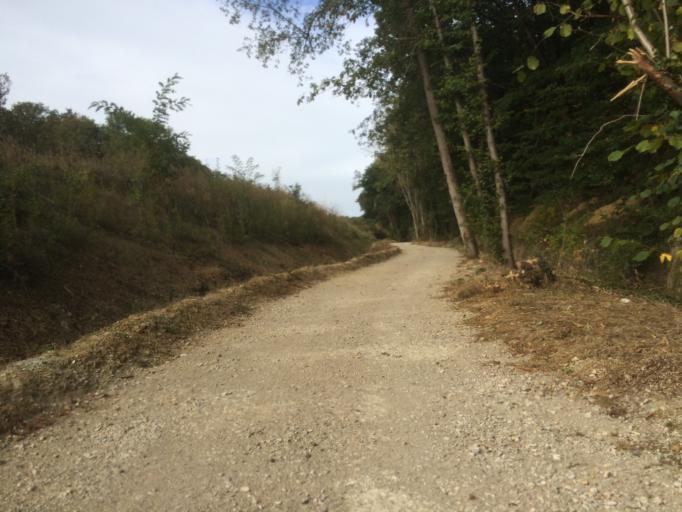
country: FR
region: Ile-de-France
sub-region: Departement des Yvelines
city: Bonnelles
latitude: 48.6275
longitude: 2.0324
